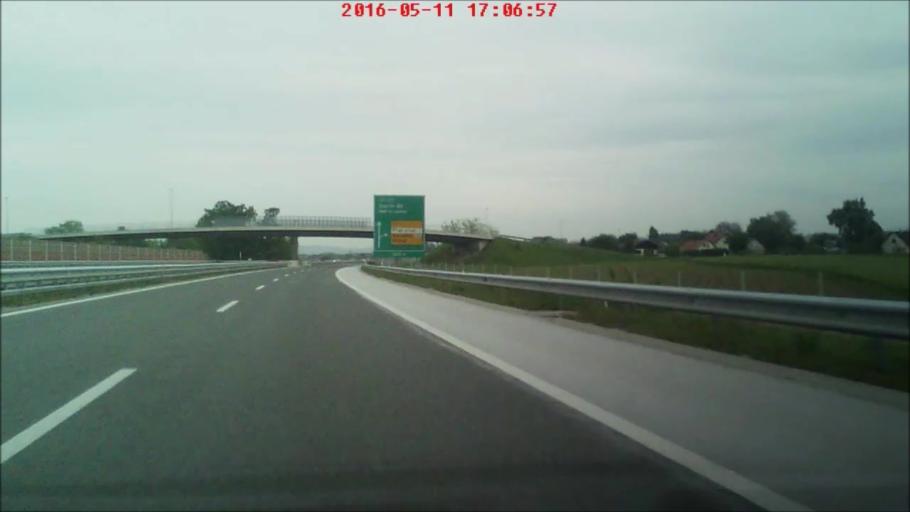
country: SI
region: Hajdina
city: Spodnja Hajdina
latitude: 46.3989
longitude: 15.8387
